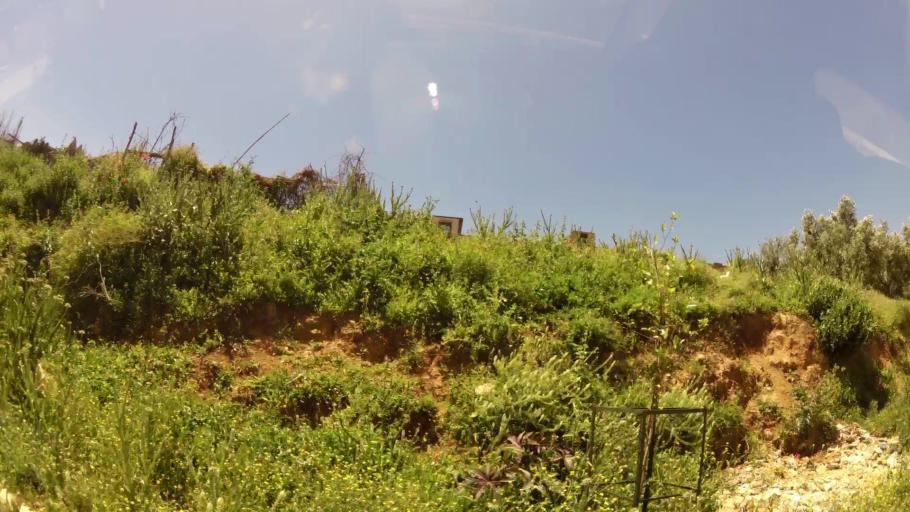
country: MA
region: Meknes-Tafilalet
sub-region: Meknes
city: Meknes
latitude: 33.8553
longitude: -5.5560
